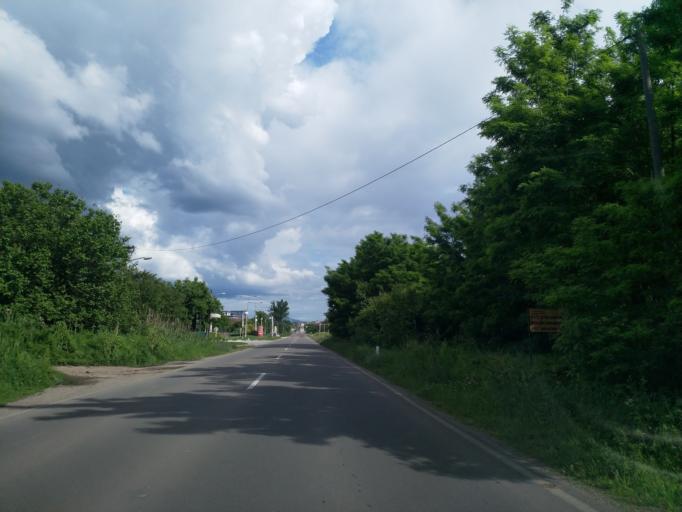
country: RS
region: Central Serbia
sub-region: Pomoravski Okrug
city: Paracin
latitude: 43.8769
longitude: 21.3940
